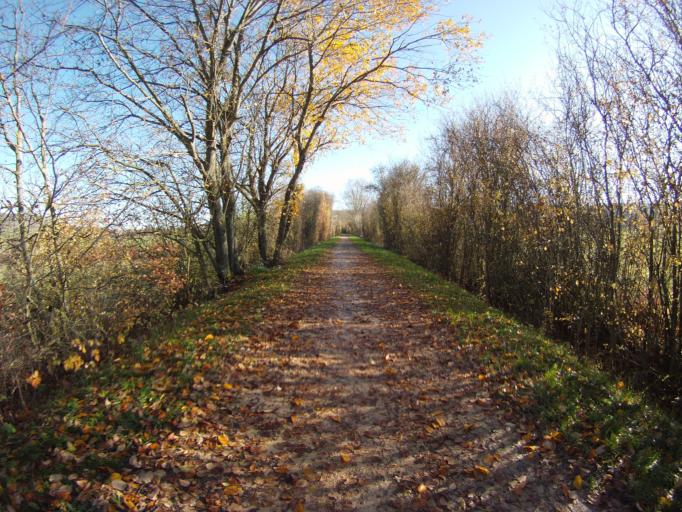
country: FR
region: Lorraine
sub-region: Departement de Meurthe-et-Moselle
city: Faulx
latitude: 48.7919
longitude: 6.2178
